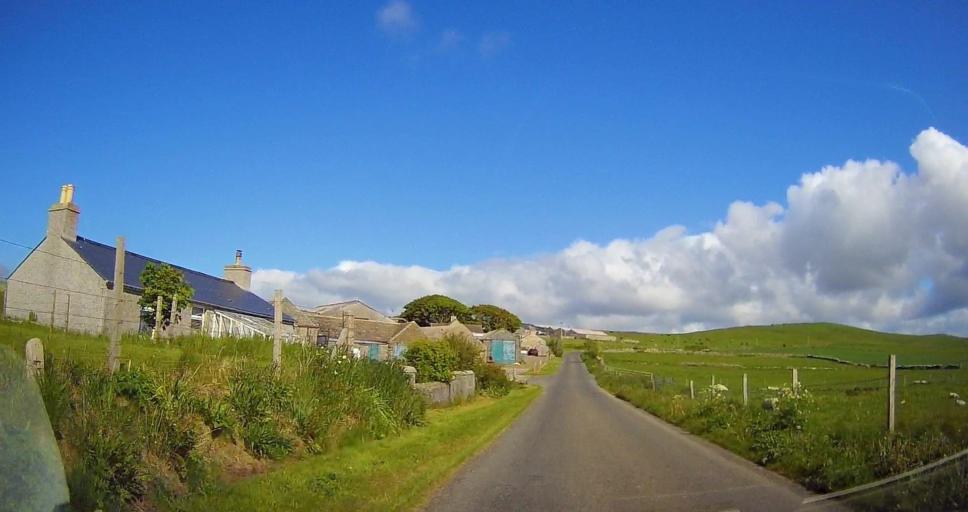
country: GB
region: Scotland
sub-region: Orkney Islands
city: Stromness
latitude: 58.9831
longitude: -3.1434
